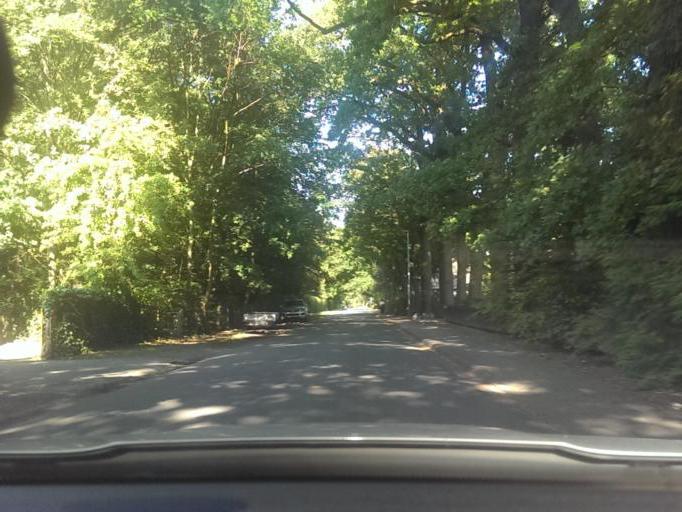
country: DE
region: Lower Saxony
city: Elze
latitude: 52.5331
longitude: 9.7550
